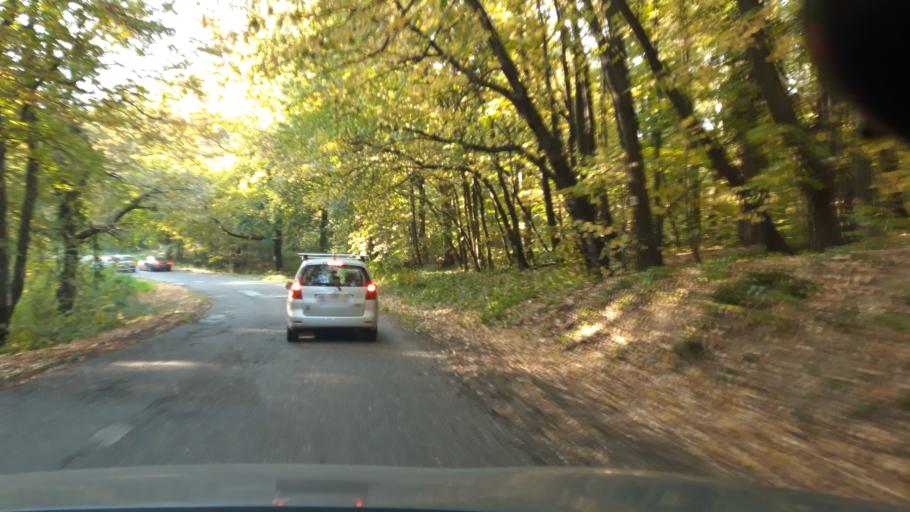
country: RS
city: Vrdnik
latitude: 45.1570
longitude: 19.7950
